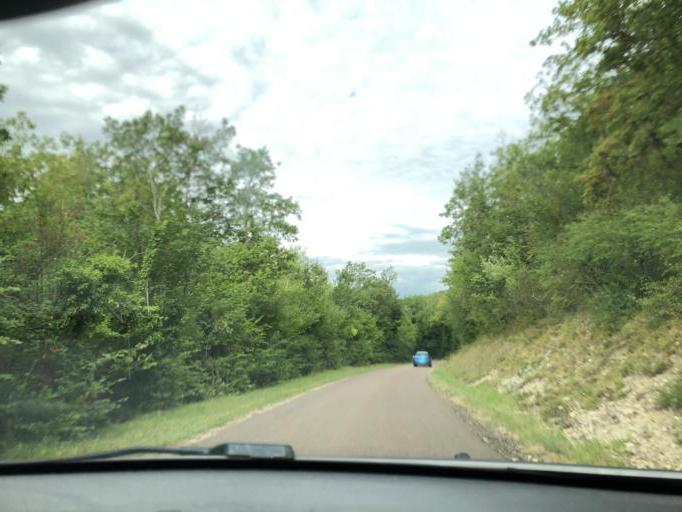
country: FR
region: Bourgogne
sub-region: Departement de l'Yonne
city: Chablis
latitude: 47.7783
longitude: 3.8234
